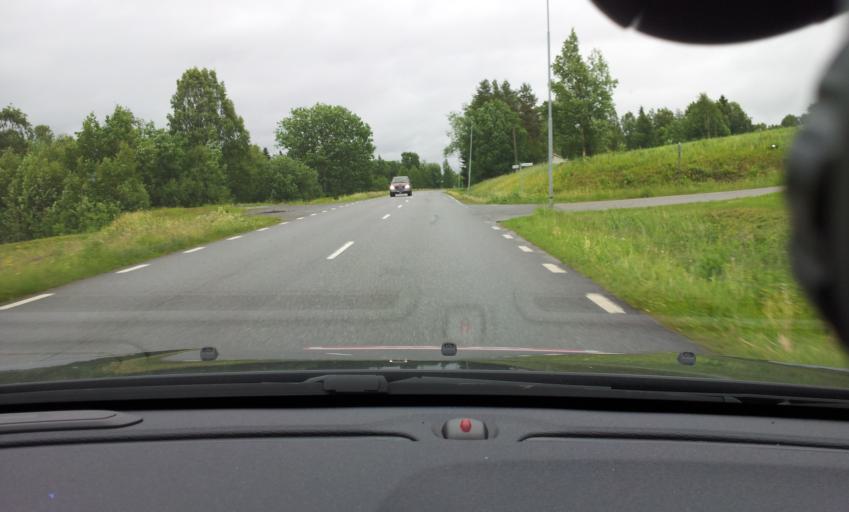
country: SE
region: Jaemtland
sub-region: Stroemsunds Kommun
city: Stroemsund
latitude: 63.5772
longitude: 15.3707
